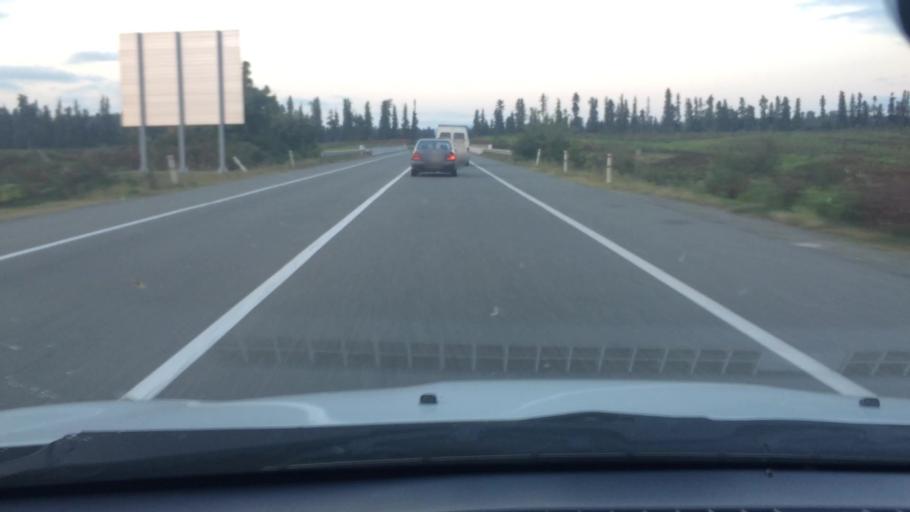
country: GE
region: Ajaria
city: Ochkhamuri
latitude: 41.8356
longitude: 41.8241
